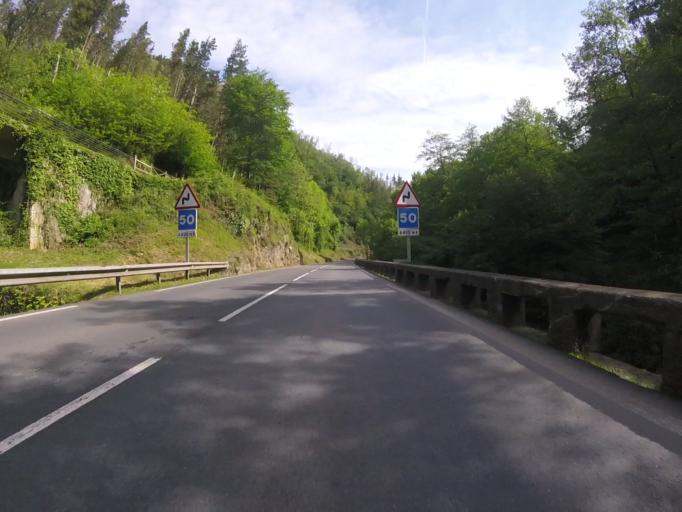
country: ES
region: Basque Country
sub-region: Provincia de Guipuzcoa
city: Anzuola
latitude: 43.1388
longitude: -2.3510
